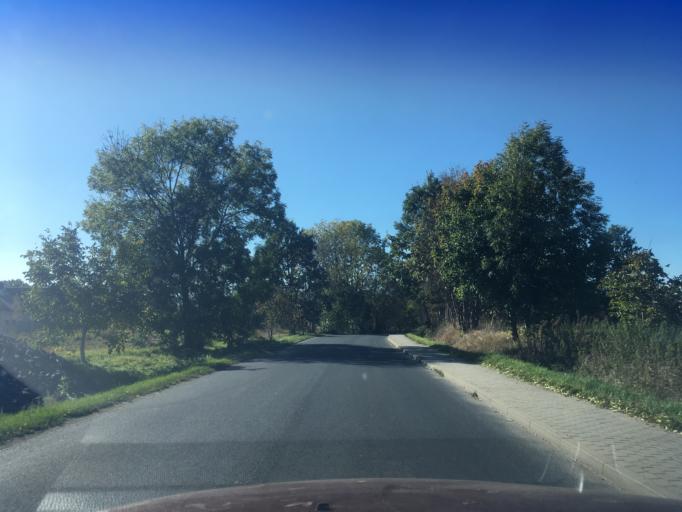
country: DE
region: Saxony
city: Zittau
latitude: 50.8889
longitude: 14.8308
